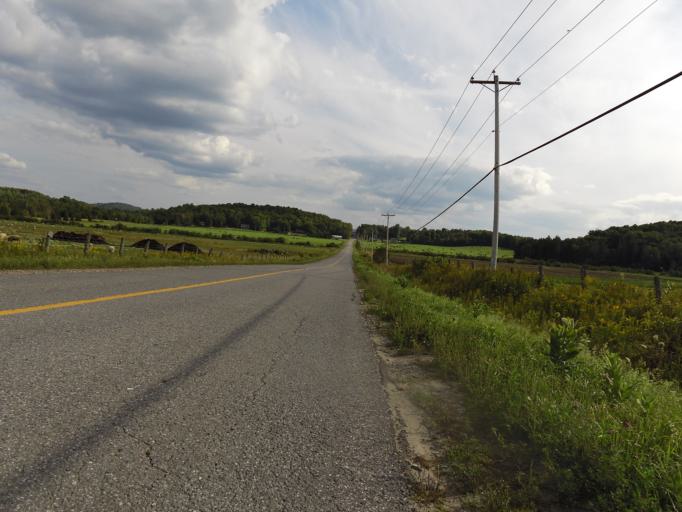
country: CA
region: Quebec
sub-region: Outaouais
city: Wakefield
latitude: 45.6595
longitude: -76.0176
